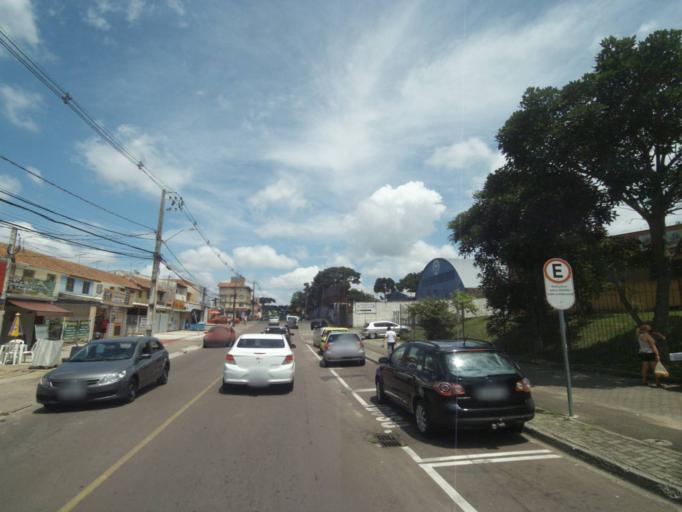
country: BR
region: Parana
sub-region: Curitiba
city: Curitiba
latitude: -25.4576
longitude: -49.3475
